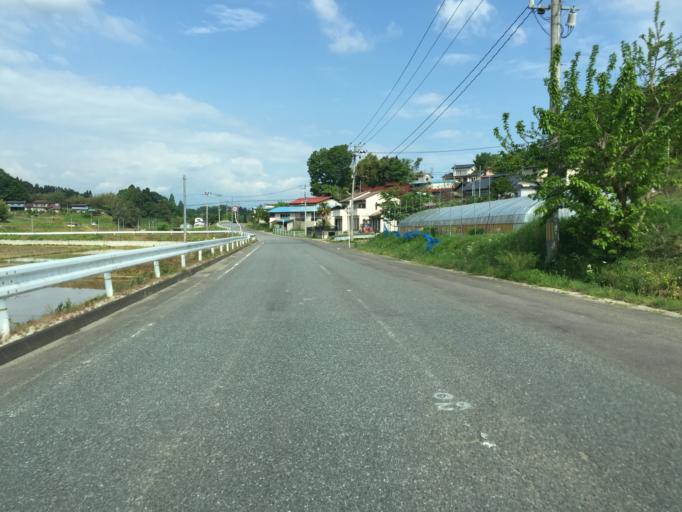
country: JP
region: Fukushima
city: Fukushima-shi
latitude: 37.6673
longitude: 140.4938
